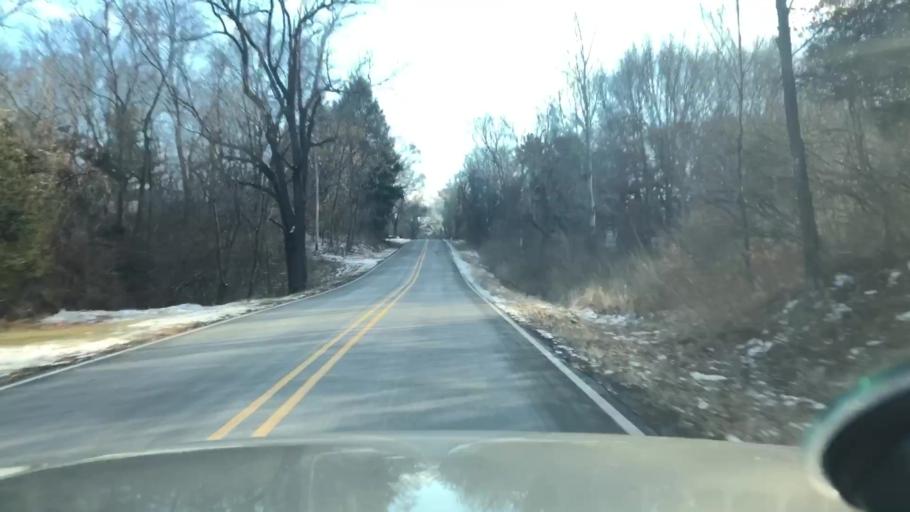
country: US
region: Michigan
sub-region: Jackson County
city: Vandercook Lake
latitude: 42.1554
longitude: -84.4521
